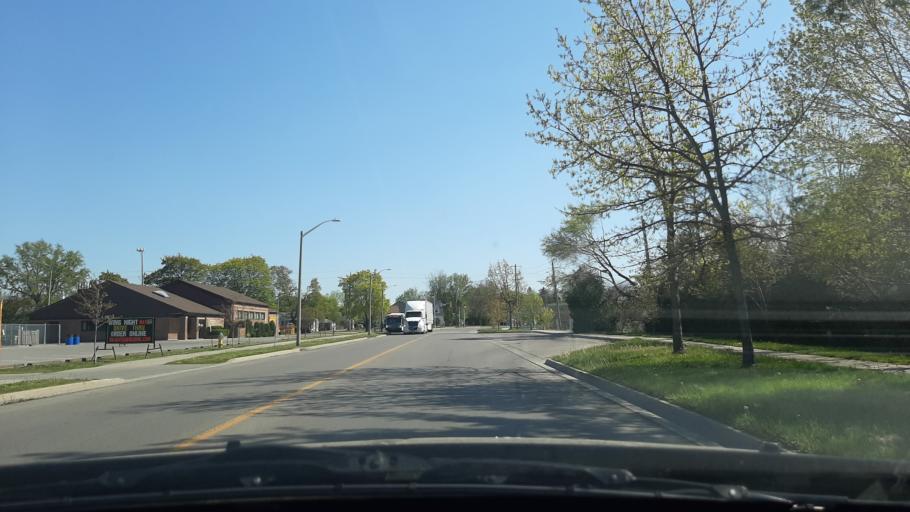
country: CA
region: Ontario
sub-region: Regional Municipality of Niagara
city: St. Catharines
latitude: 43.2141
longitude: -79.2171
